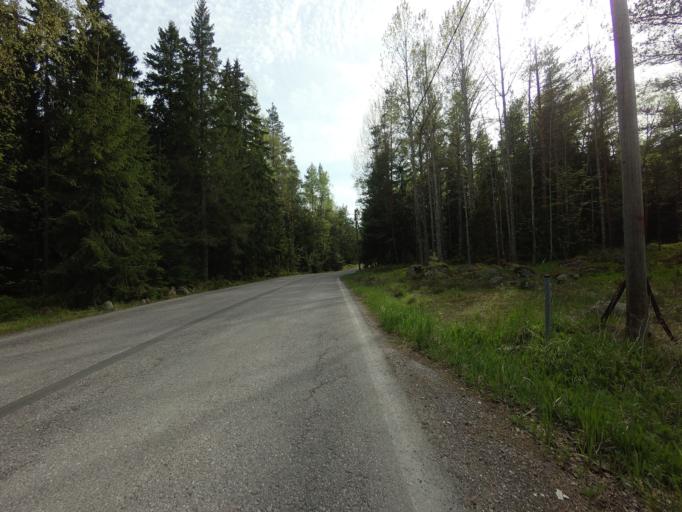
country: FI
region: Uusimaa
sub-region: Helsinki
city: Koukkuniemi
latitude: 60.1161
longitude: 24.7150
